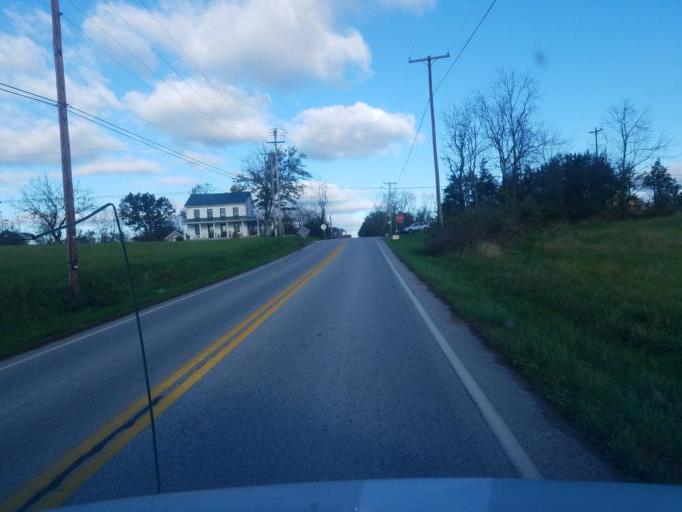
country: US
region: Pennsylvania
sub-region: Adams County
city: Gettysburg
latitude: 39.8541
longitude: -77.2534
